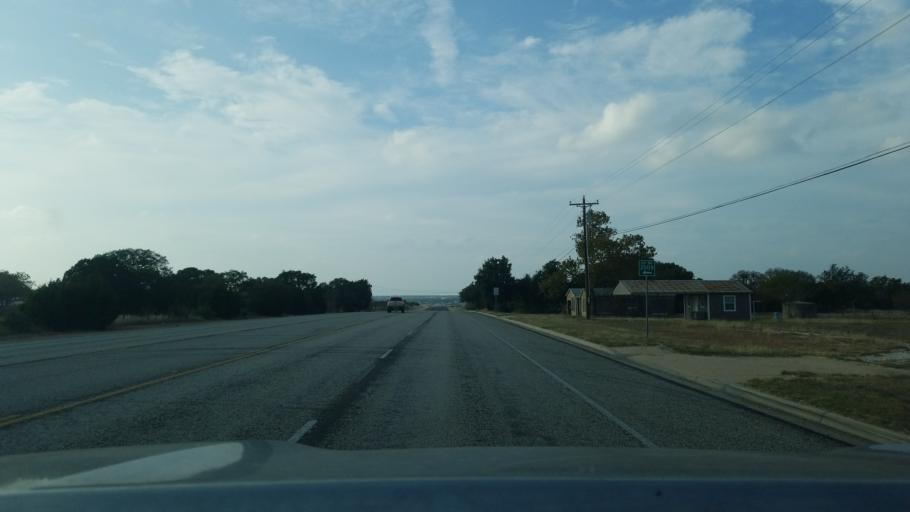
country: US
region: Texas
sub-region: Lampasas County
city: Lampasas
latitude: 31.2240
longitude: -98.4004
